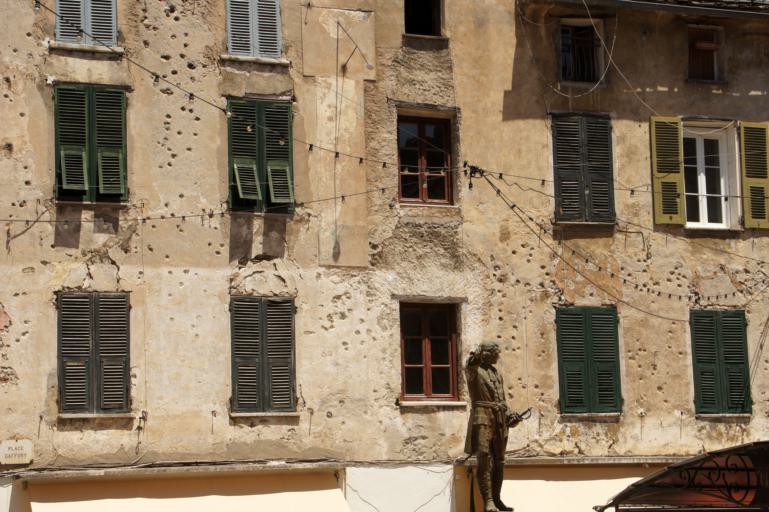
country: FR
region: Corsica
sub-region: Departement de la Haute-Corse
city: Corte
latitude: 42.3043
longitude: 9.1490
